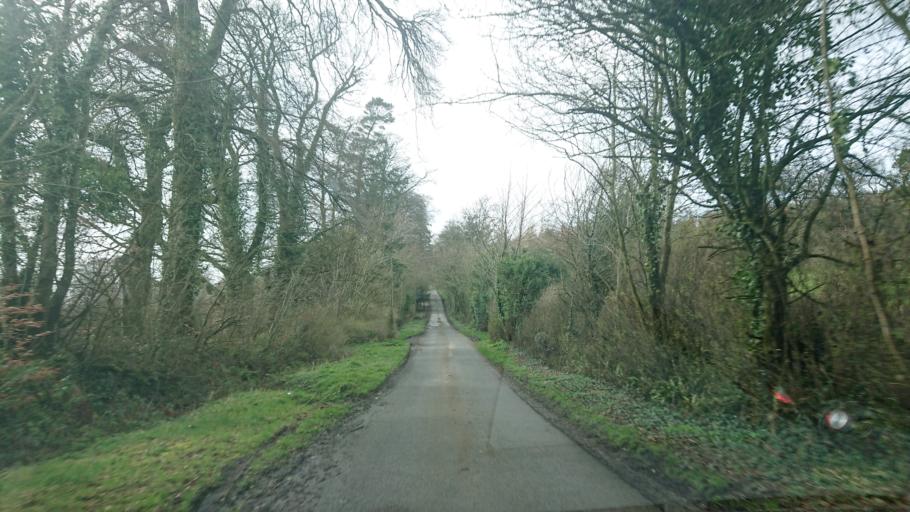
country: IE
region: Leinster
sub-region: Kildare
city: Eadestown
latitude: 53.1581
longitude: -6.5798
